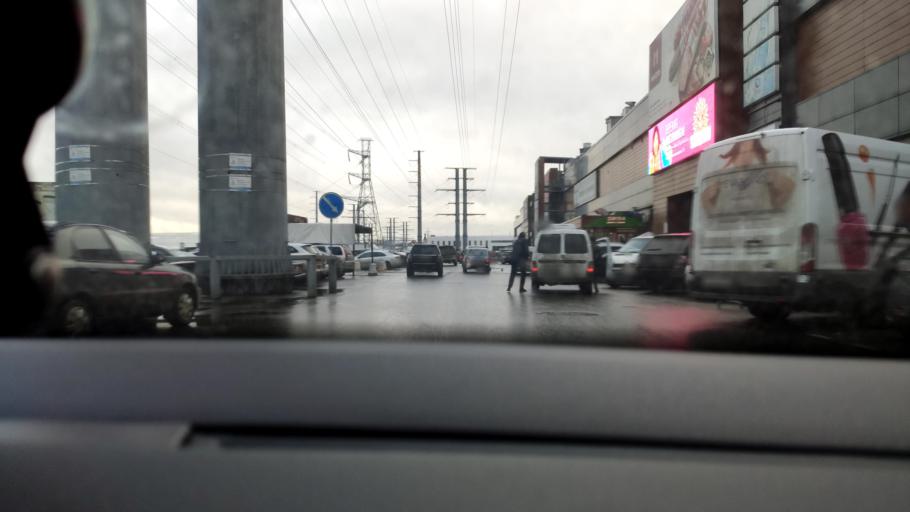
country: RU
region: Moskovskaya
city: Mosrentgen
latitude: 55.6001
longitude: 37.4700
